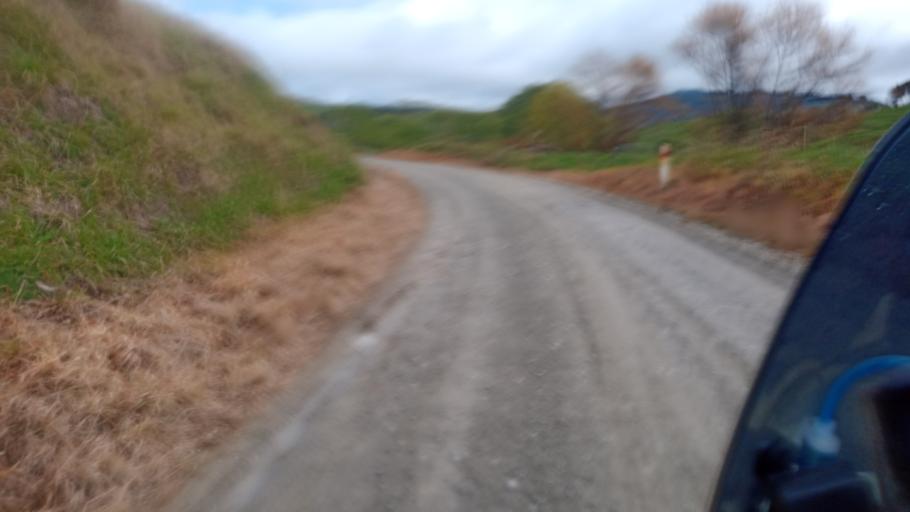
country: NZ
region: Gisborne
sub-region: Gisborne District
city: Gisborne
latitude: -38.5876
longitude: 178.1683
